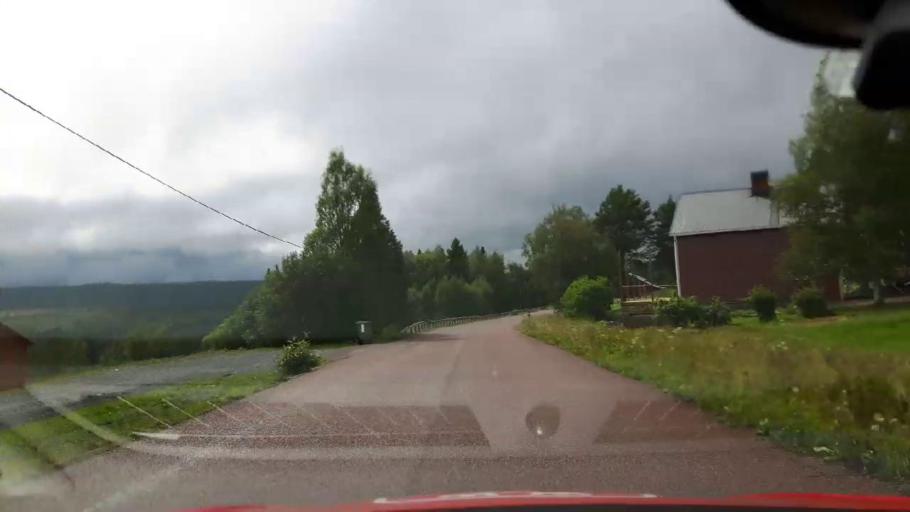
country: SE
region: Jaemtland
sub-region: Krokoms Kommun
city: Valla
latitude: 63.3842
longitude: 13.8132
